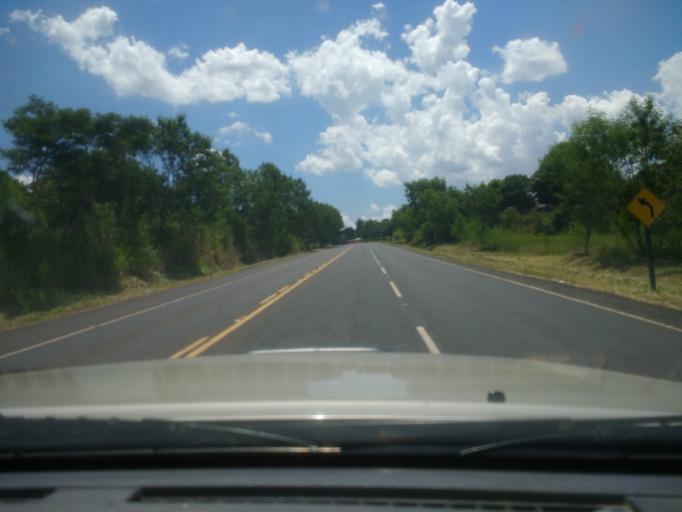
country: PY
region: San Pedro
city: Guayaybi
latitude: -24.5968
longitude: -56.5068
